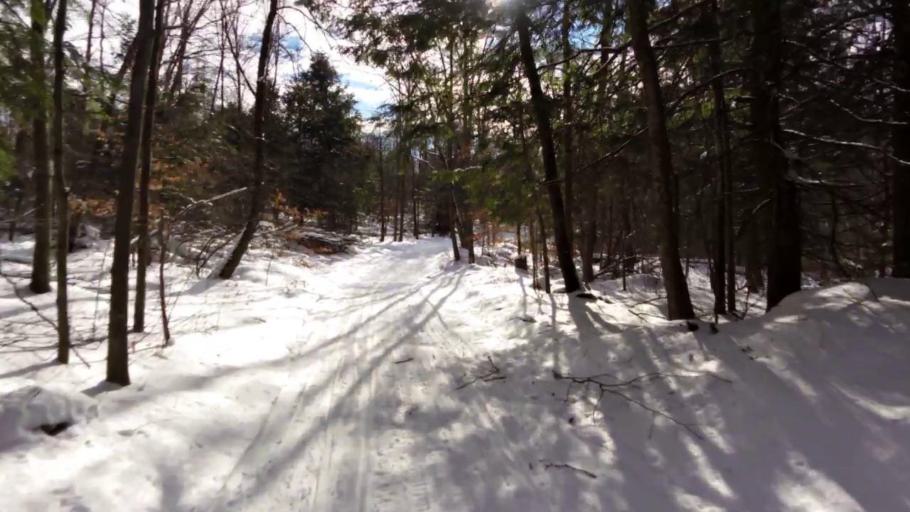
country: US
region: Pennsylvania
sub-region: McKean County
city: Foster Brook
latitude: 42.0020
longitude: -78.5408
